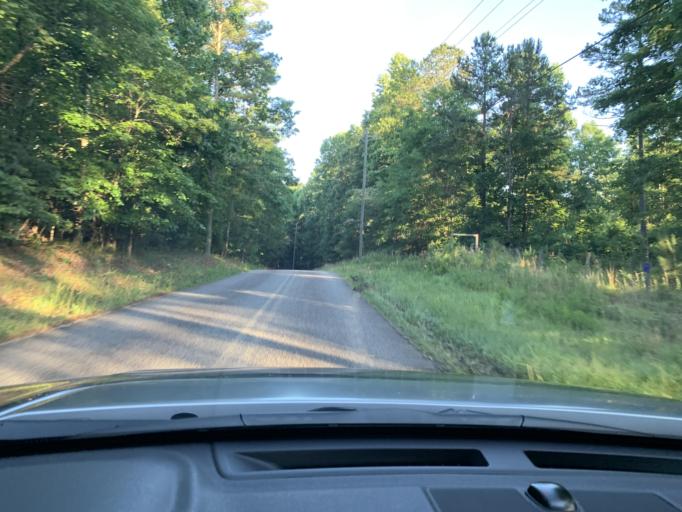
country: US
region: Georgia
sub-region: Bartow County
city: Rydal
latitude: 34.2319
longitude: -84.6421
